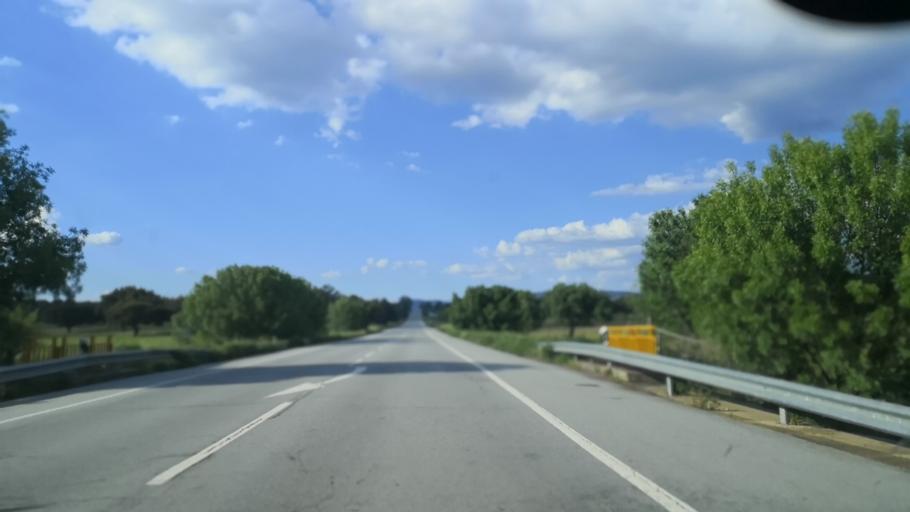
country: PT
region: Portalegre
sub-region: Portalegre
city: Urra
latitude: 39.2295
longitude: -7.4547
